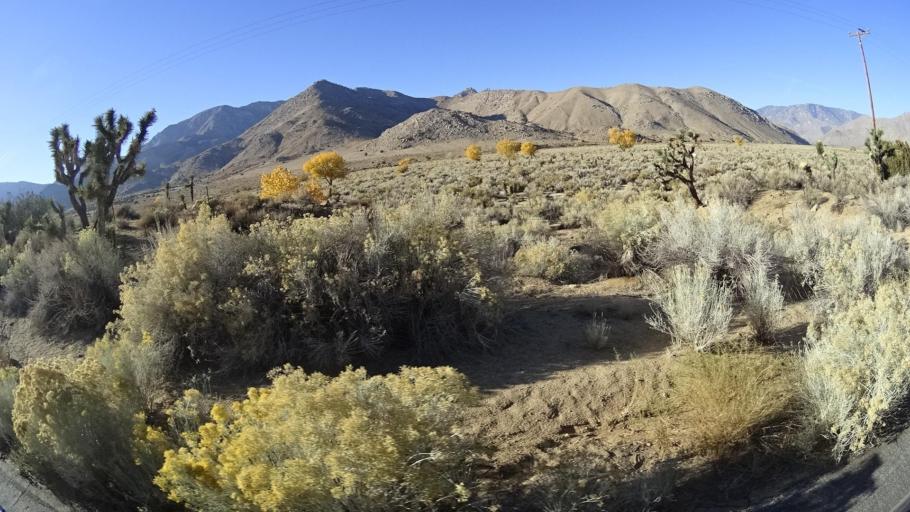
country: US
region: California
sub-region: Kern County
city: Weldon
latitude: 35.5830
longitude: -118.2444
